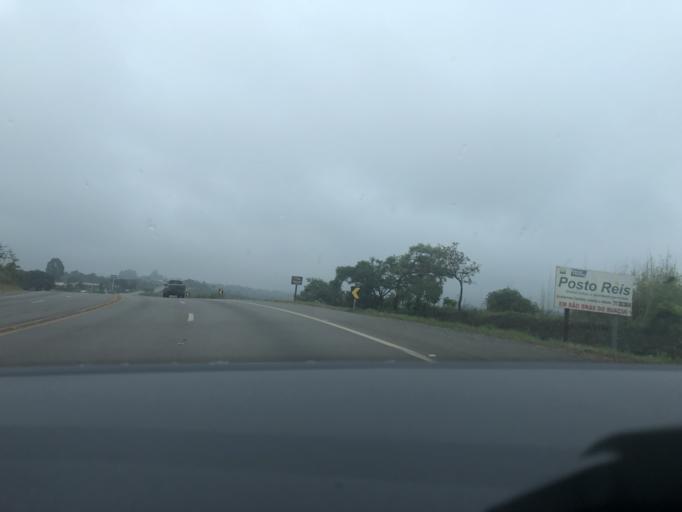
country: BR
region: Minas Gerais
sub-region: Congonhas
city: Congonhas
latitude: -20.6139
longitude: -43.9226
